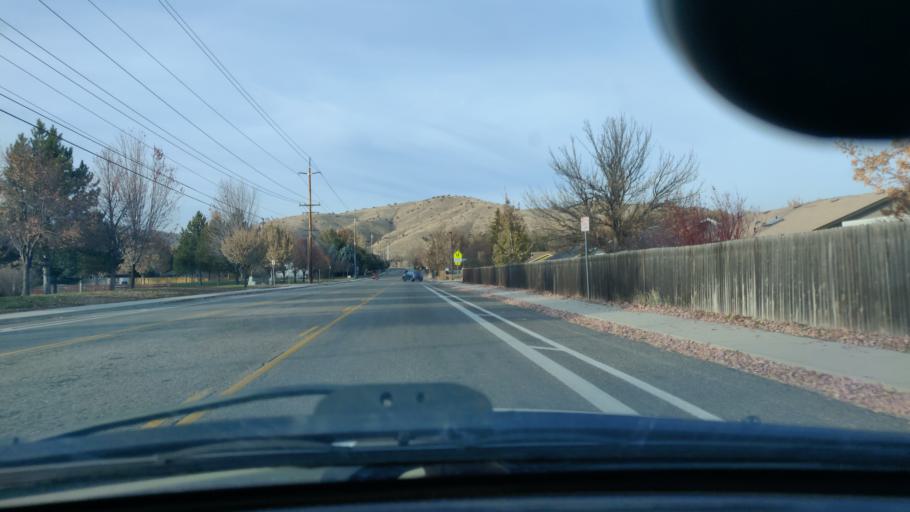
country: US
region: Idaho
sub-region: Ada County
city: Garden City
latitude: 43.6793
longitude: -116.2792
